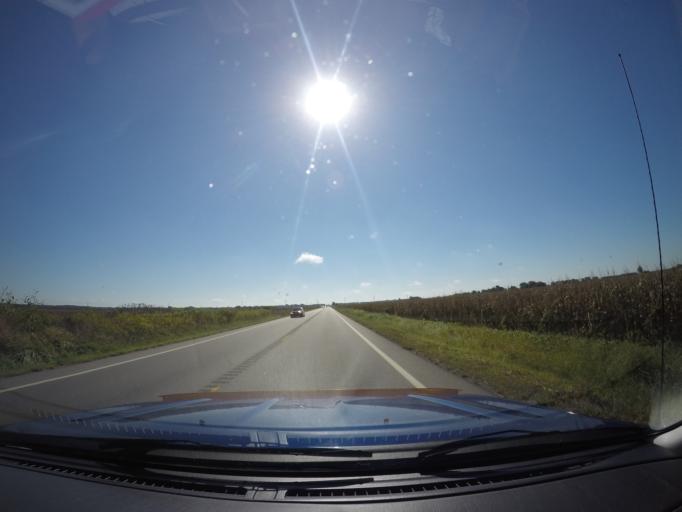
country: US
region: Kansas
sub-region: Shawnee County
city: Rossville
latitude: 39.1532
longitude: -95.9844
